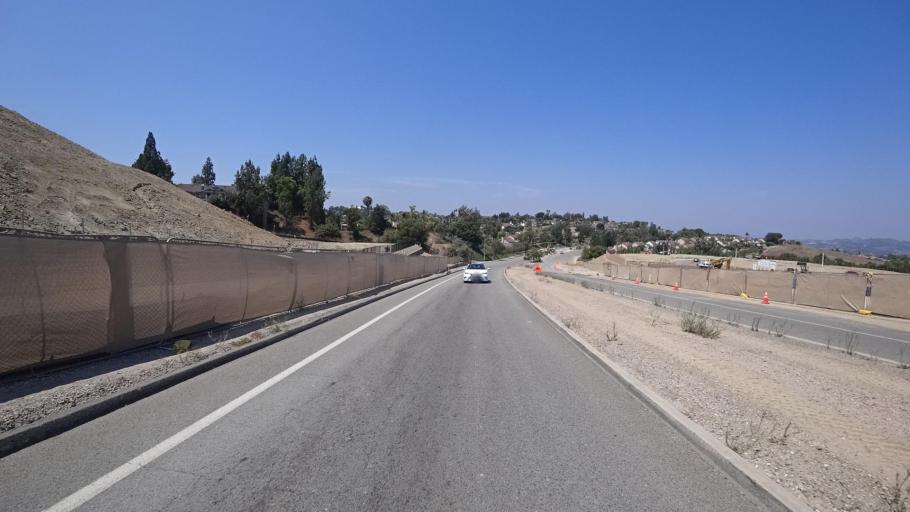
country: US
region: California
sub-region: San Diego County
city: Vista
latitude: 33.2218
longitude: -117.2611
